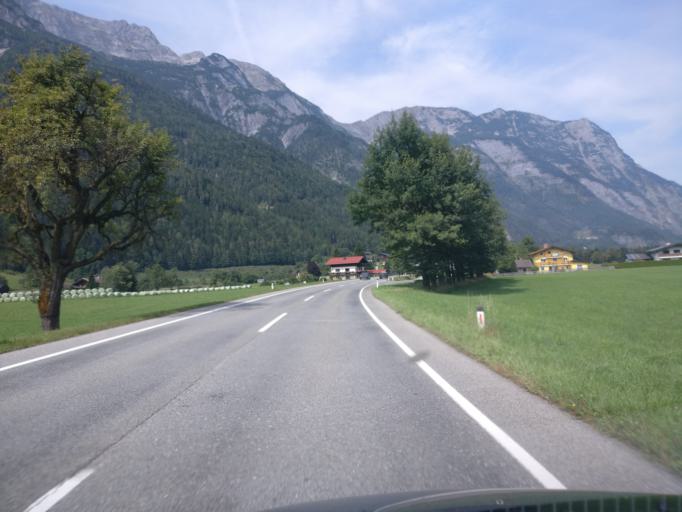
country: AT
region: Salzburg
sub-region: Politischer Bezirk Sankt Johann im Pongau
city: Werfen
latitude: 47.4984
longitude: 13.1728
